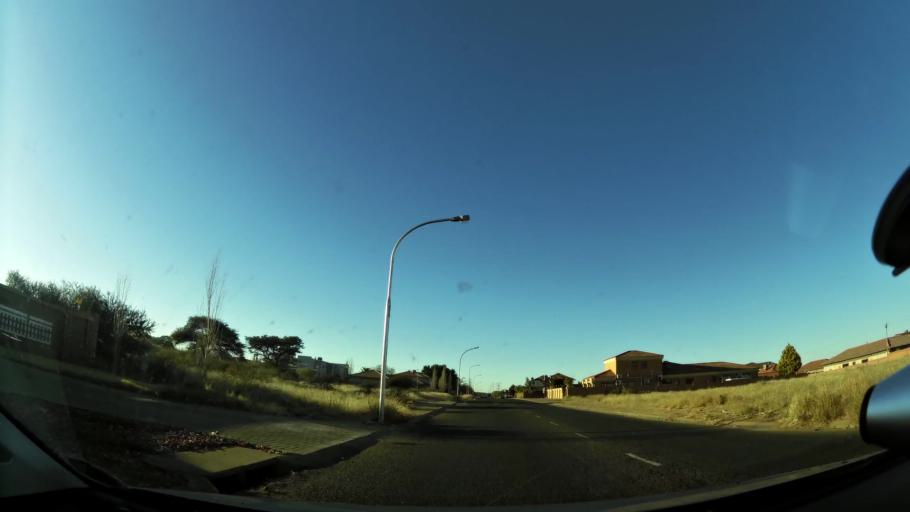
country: ZA
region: Northern Cape
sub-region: Frances Baard District Municipality
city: Kimberley
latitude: -28.7579
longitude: 24.7402
